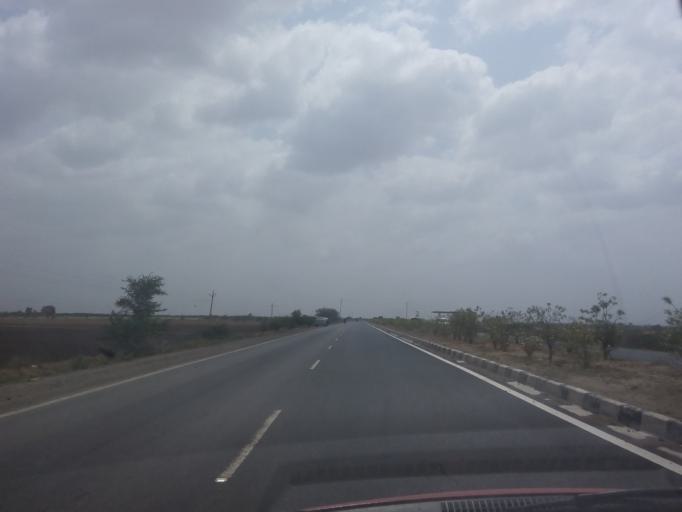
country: IN
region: Gujarat
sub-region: Surendranagar
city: Lakhtar
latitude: 23.0520
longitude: 71.7153
